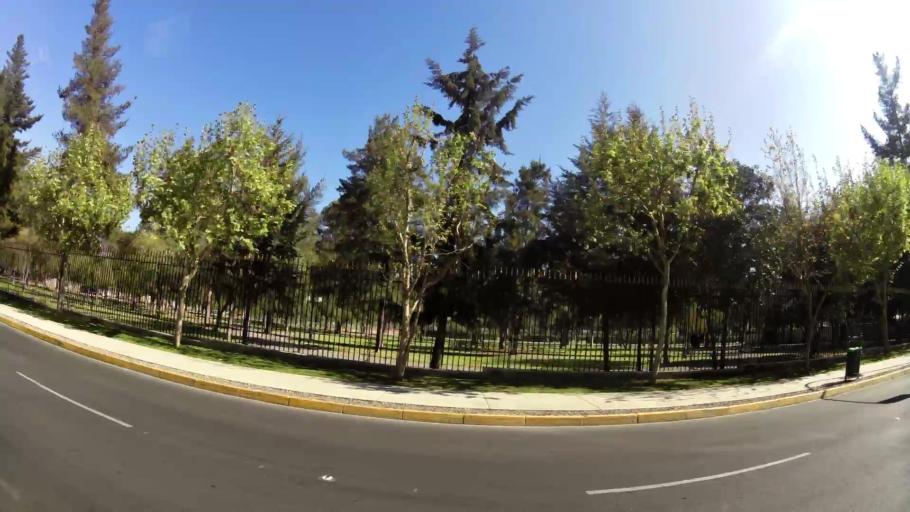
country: CL
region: Santiago Metropolitan
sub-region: Provincia de Santiago
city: Villa Presidente Frei, Nunoa, Santiago, Chile
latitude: -33.4107
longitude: -70.5792
